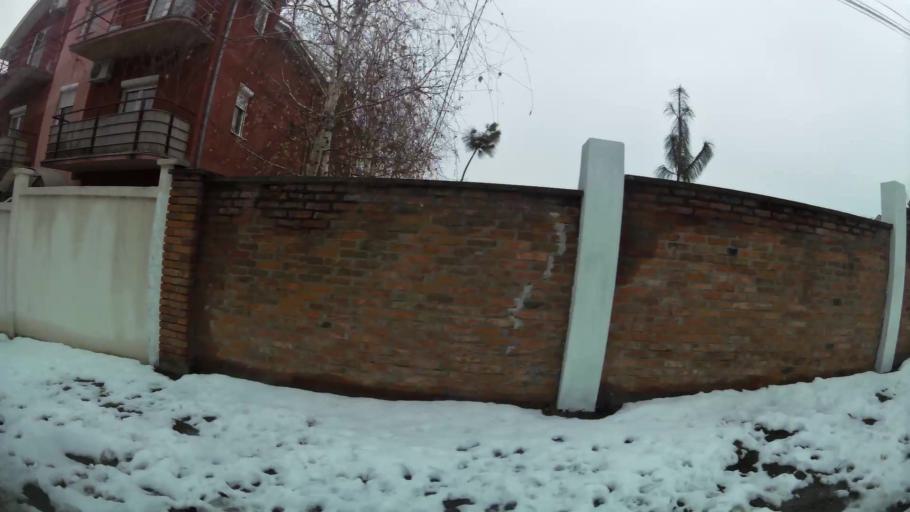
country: RS
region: Central Serbia
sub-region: Belgrade
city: Zvezdara
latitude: 44.7444
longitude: 20.5024
